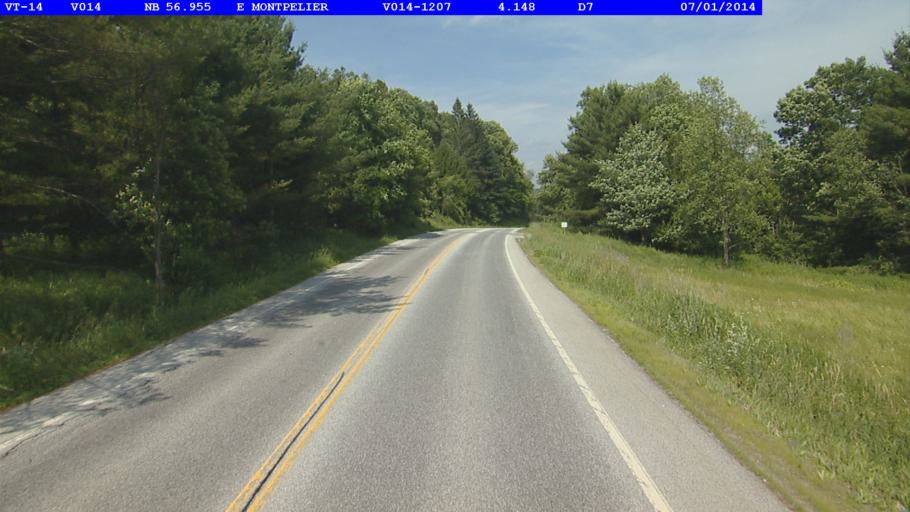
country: US
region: Vermont
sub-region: Washington County
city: Barre
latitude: 44.2882
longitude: -72.4631
